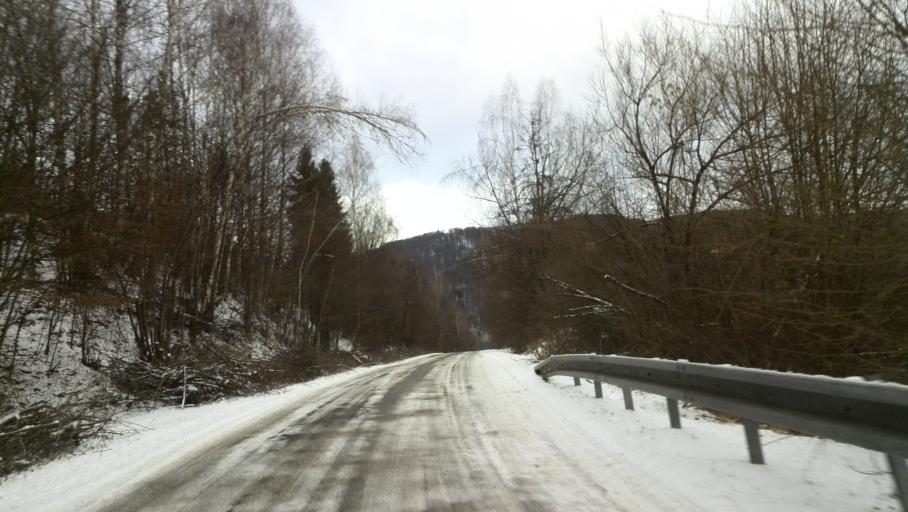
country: SK
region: Kosicky
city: Gelnica
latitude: 48.8269
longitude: 21.0664
